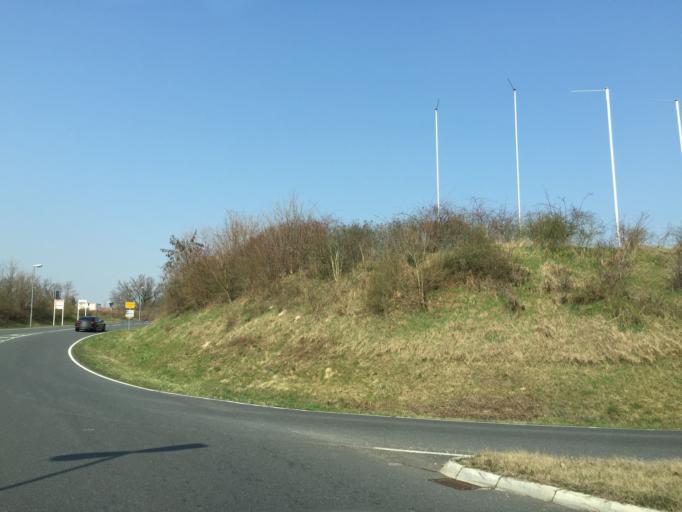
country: DE
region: Baden-Wuerttemberg
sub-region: Karlsruhe Region
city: Bruhl
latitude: 49.4018
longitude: 8.5605
